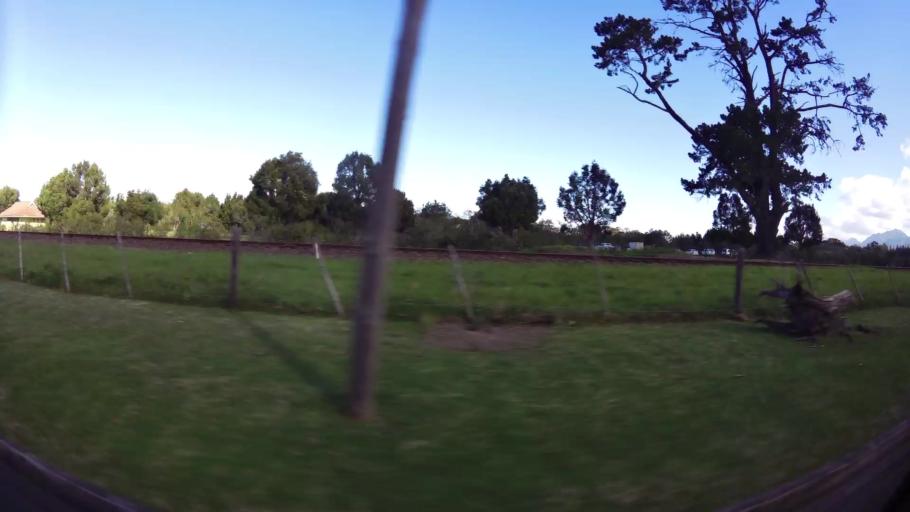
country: ZA
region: Western Cape
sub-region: Eden District Municipality
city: George
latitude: -33.9448
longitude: 22.4649
